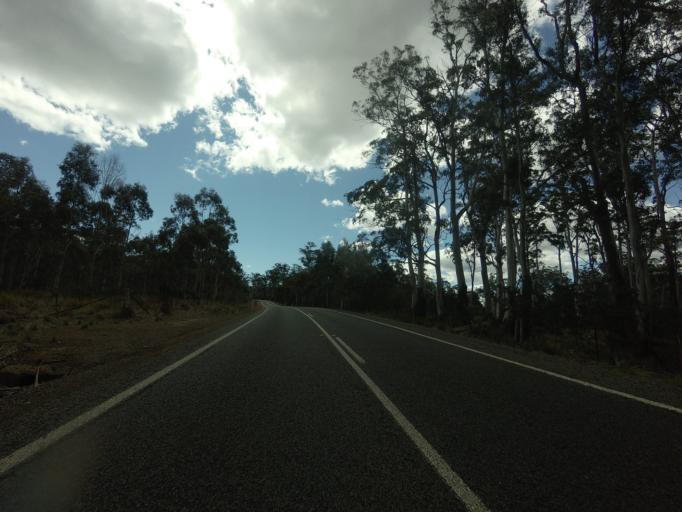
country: AU
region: Tasmania
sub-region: Northern Midlands
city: Evandale
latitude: -41.9671
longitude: 147.6435
